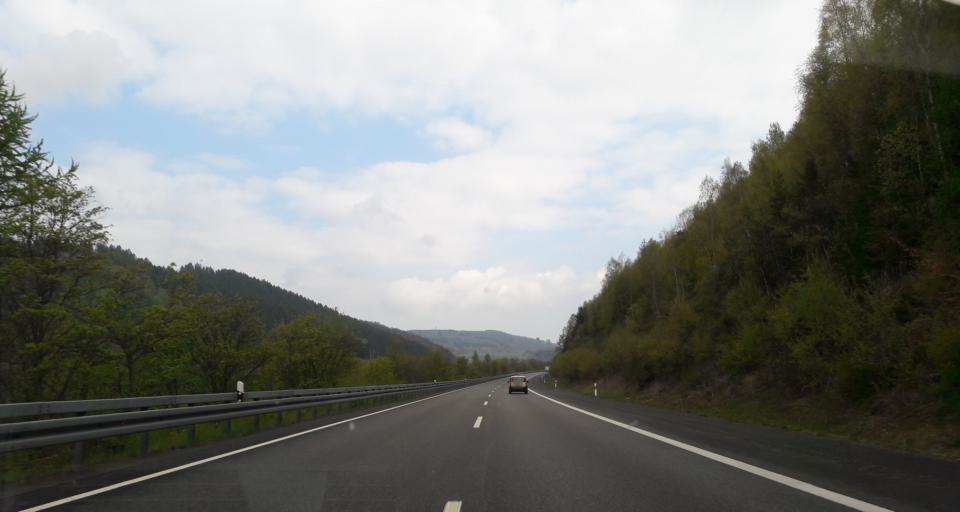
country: DE
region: Saarland
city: Nonnweiler
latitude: 49.5570
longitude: 6.9722
